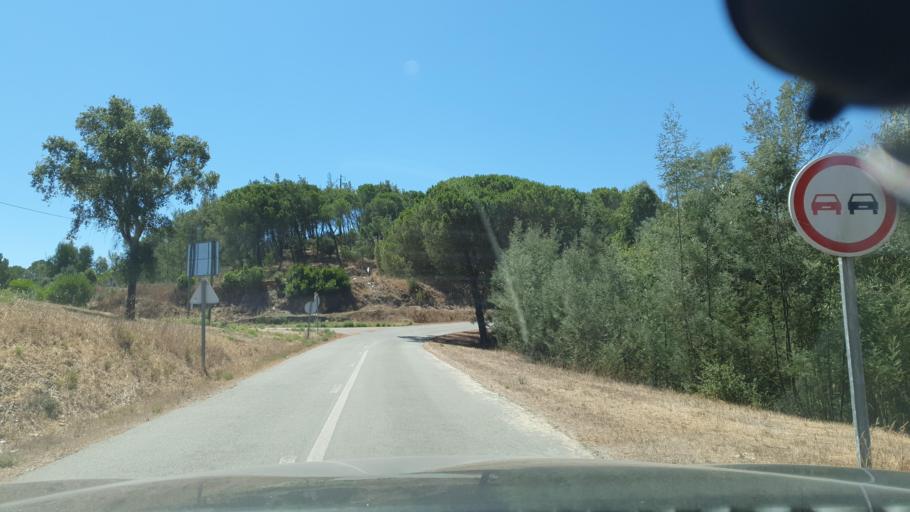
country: PT
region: Beja
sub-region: Odemira
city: Odemira
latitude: 37.5067
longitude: -8.4364
